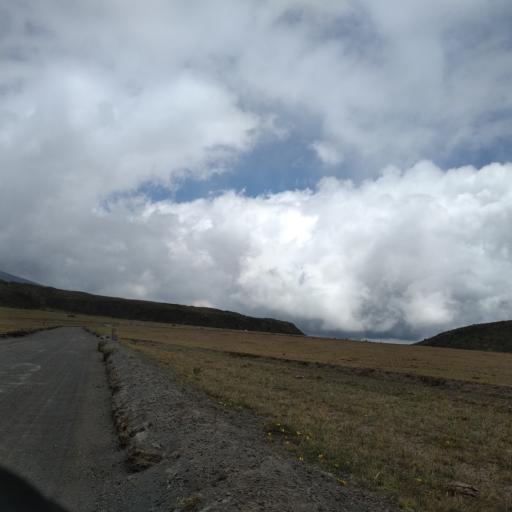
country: EC
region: Pichincha
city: Machachi
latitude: -0.6233
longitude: -78.4745
